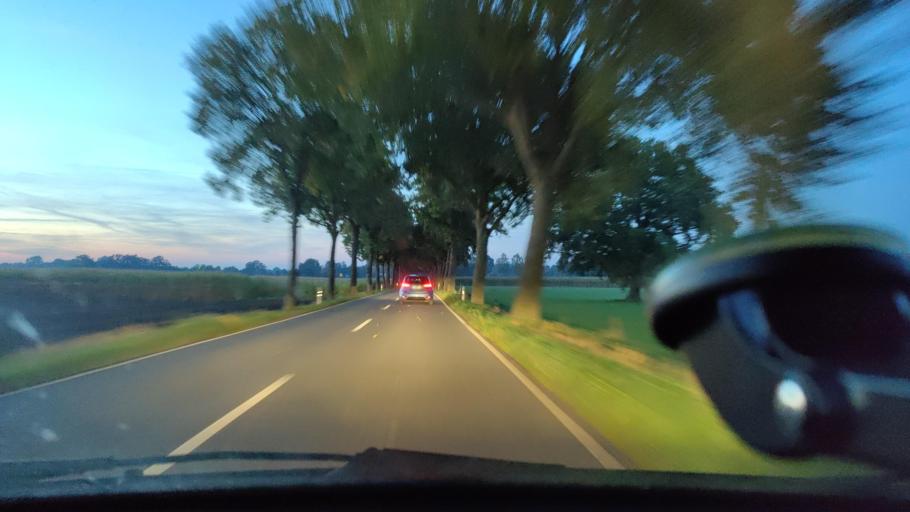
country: DE
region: North Rhine-Westphalia
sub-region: Regierungsbezirk Munster
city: Sudlohn
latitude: 51.9165
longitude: 6.8514
